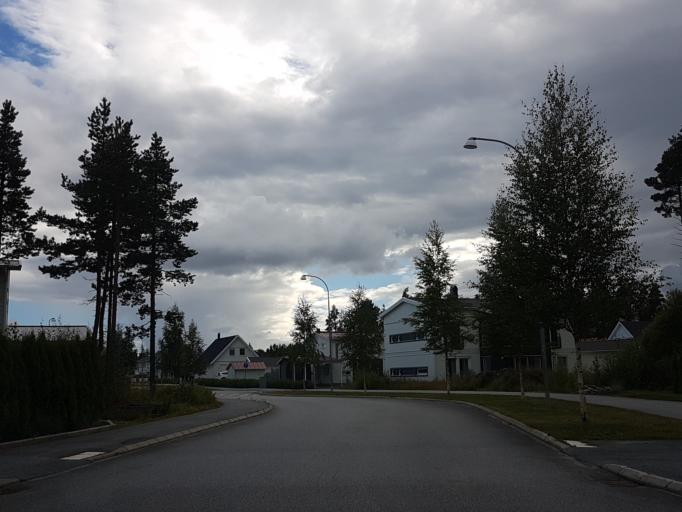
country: SE
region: Vaesterbotten
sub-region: Umea Kommun
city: Ersmark
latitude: 63.8048
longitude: 20.3698
